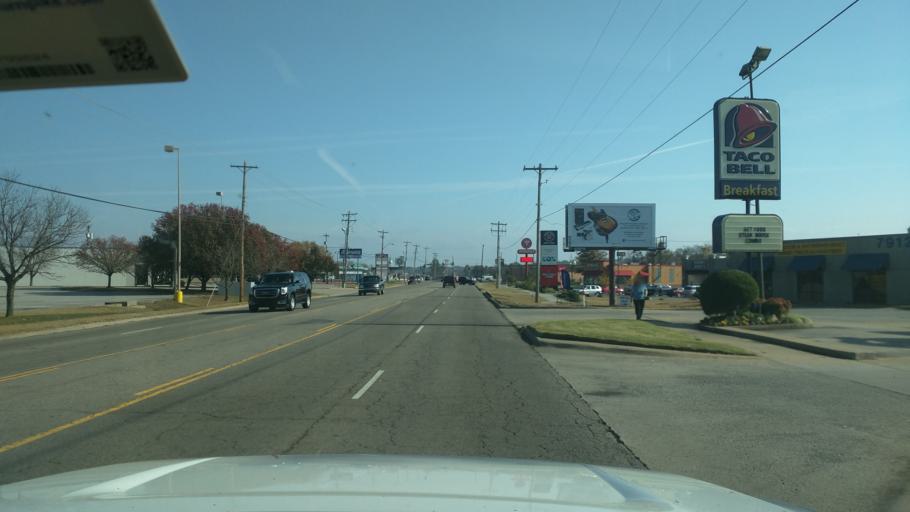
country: US
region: Arkansas
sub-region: Sebastian County
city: Barling
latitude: 35.3496
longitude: -94.3438
